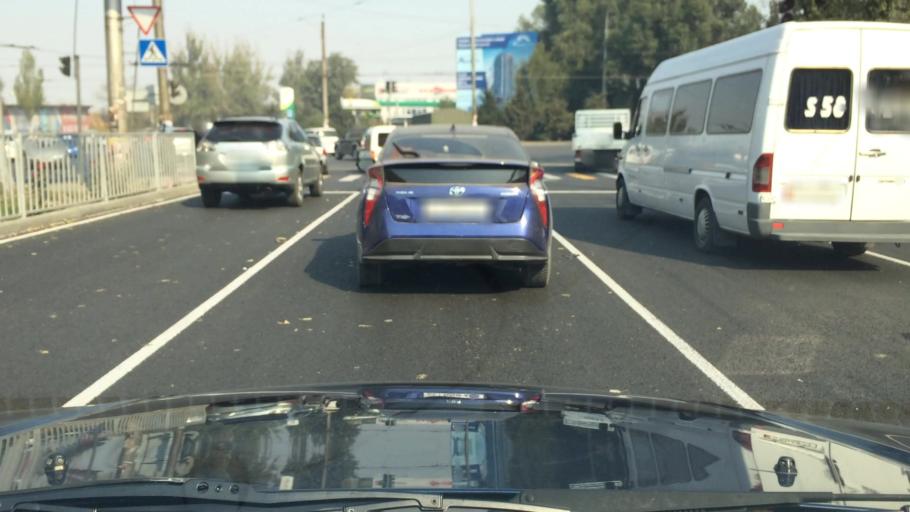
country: KG
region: Chuy
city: Lebedinovka
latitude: 42.8745
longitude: 74.6374
